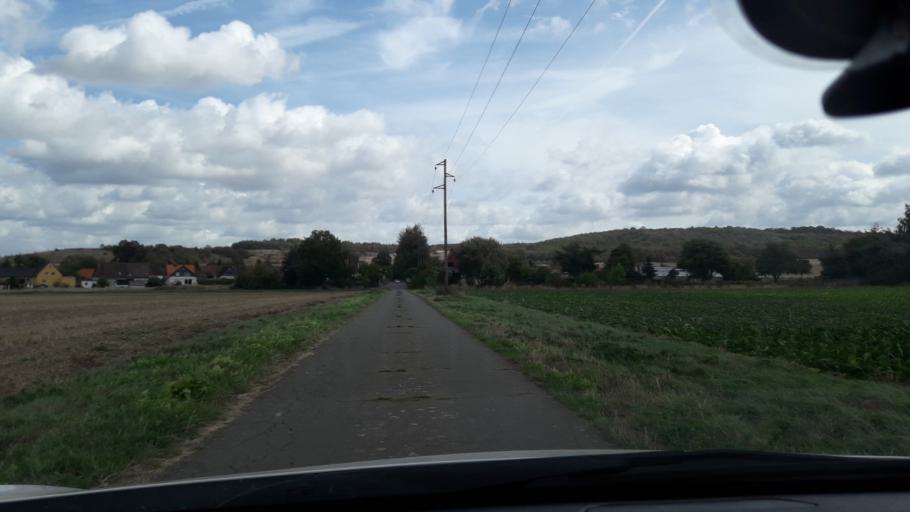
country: DE
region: Lower Saxony
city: Liebenburg
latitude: 51.9949
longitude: 10.3947
